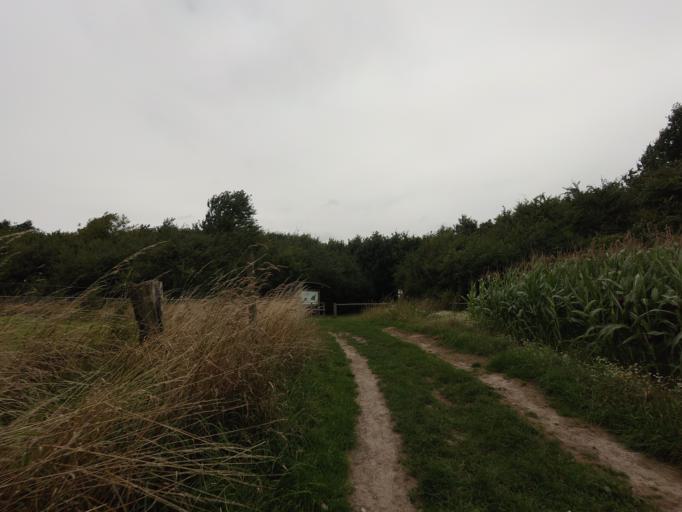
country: BE
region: Flanders
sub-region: Provincie Vlaams-Brabant
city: Grimbergen
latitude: 50.9440
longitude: 4.3801
